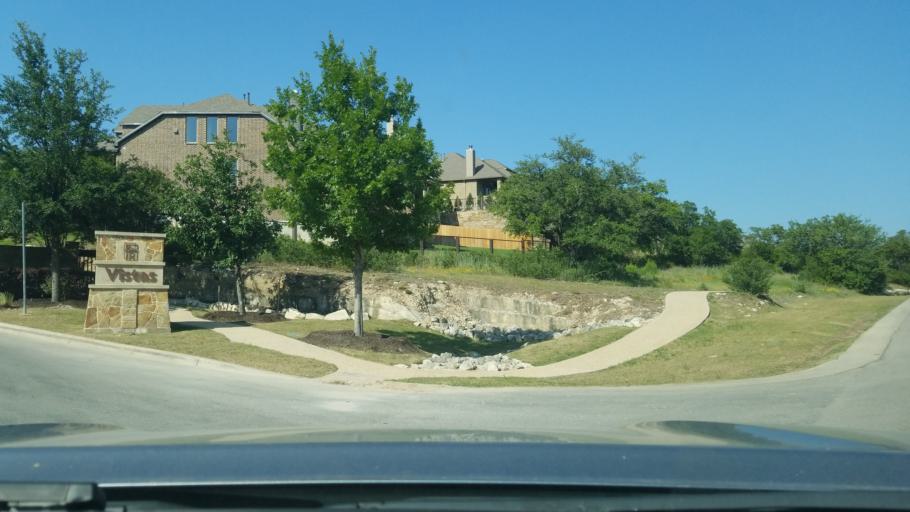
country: US
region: Texas
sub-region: Comal County
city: Bulverde
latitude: 29.7693
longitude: -98.4241
